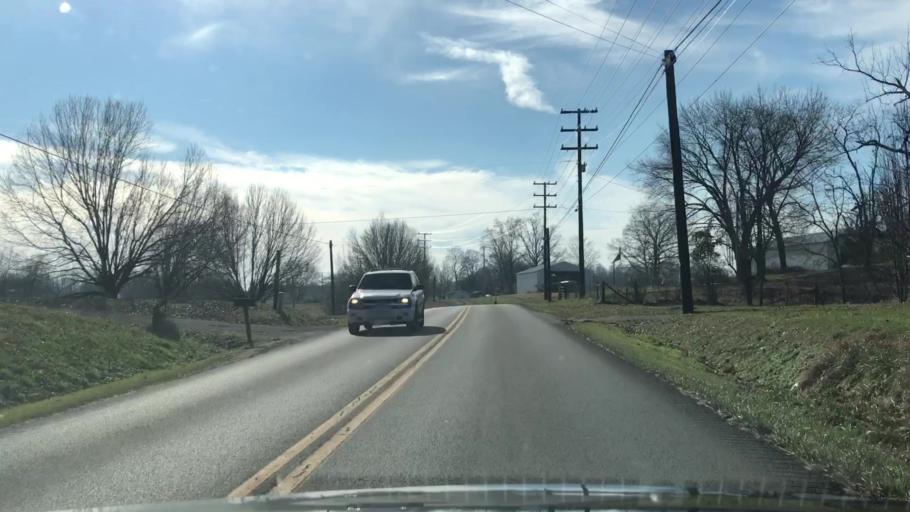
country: US
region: Kentucky
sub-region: Metcalfe County
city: Edmonton
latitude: 36.9611
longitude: -85.6121
